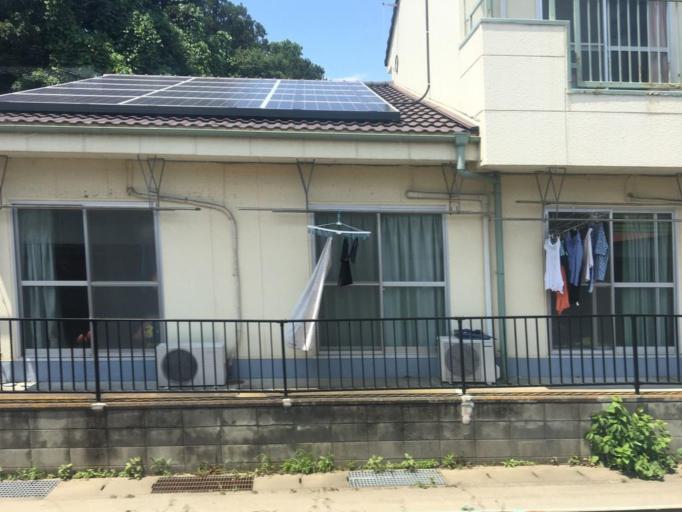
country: JP
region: Gunma
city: Omamacho-omama
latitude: 36.4198
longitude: 139.2632
